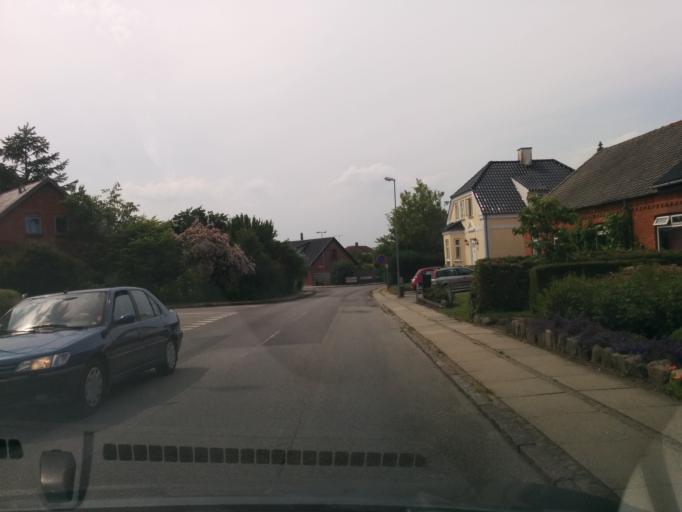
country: DK
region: Central Jutland
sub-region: Arhus Kommune
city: Malling
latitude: 56.0382
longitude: 10.1966
